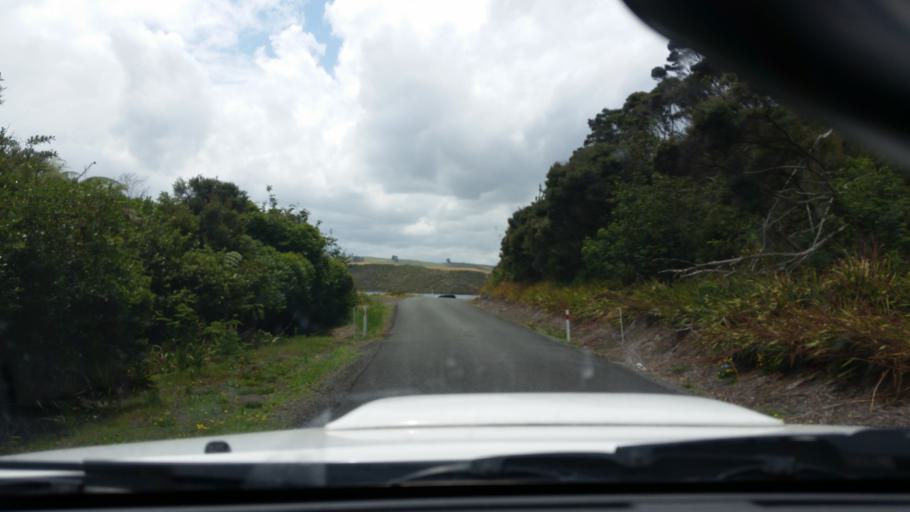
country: NZ
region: Northland
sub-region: Kaipara District
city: Dargaville
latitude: -35.7988
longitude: 173.6246
